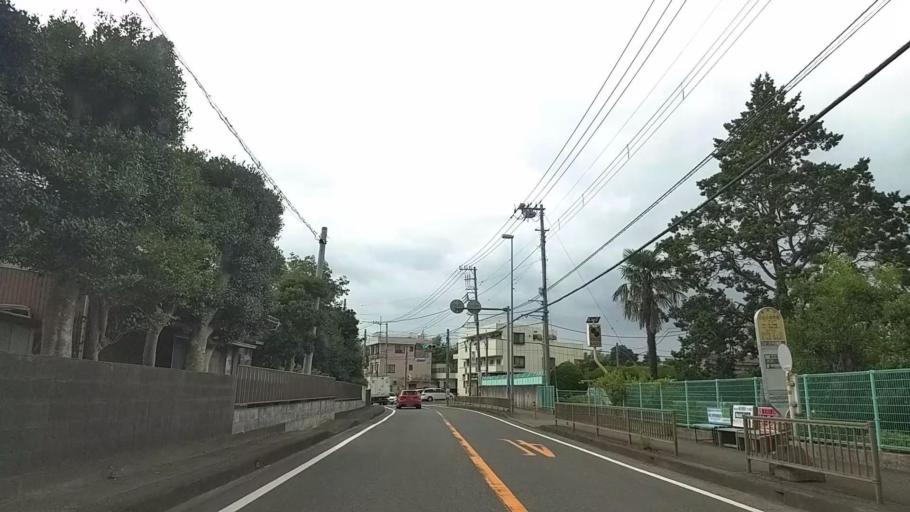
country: JP
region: Kanagawa
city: Chigasaki
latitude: 35.3712
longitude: 139.4233
